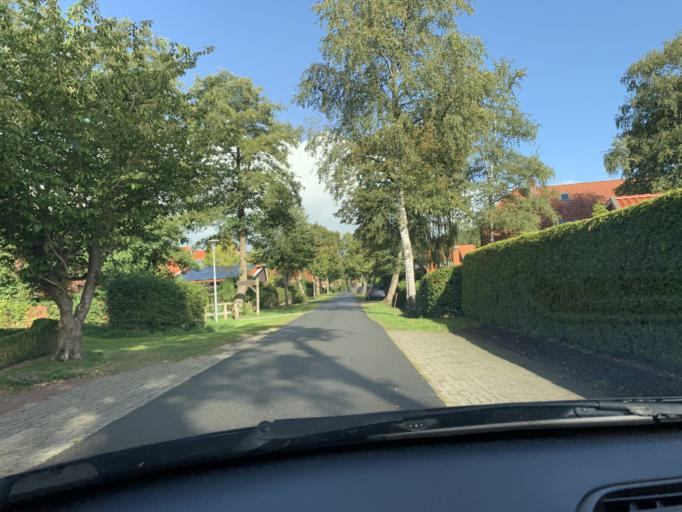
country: DE
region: Lower Saxony
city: Westerstede
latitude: 53.2352
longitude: 7.8823
